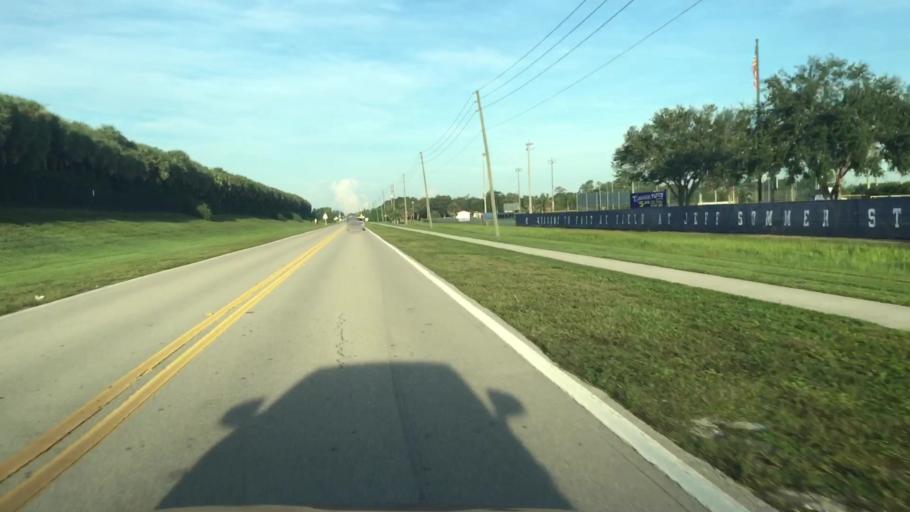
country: US
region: Florida
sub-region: Lee County
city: Estero
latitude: 26.4204
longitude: -81.7984
